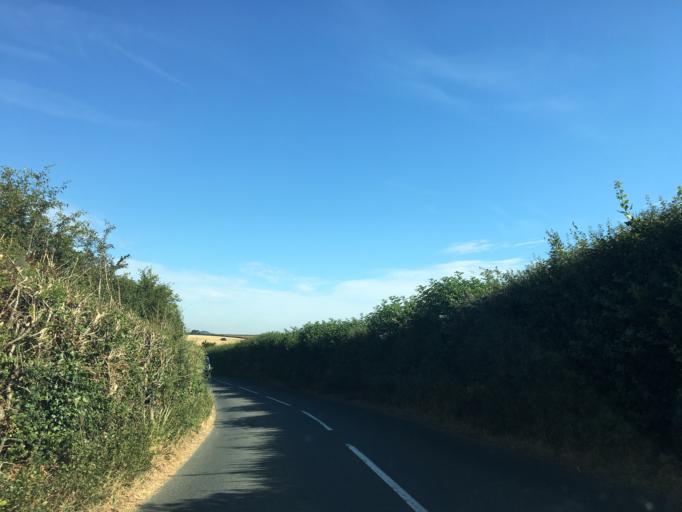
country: GB
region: England
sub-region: Isle of Wight
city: Niton
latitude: 50.6168
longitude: -1.2816
